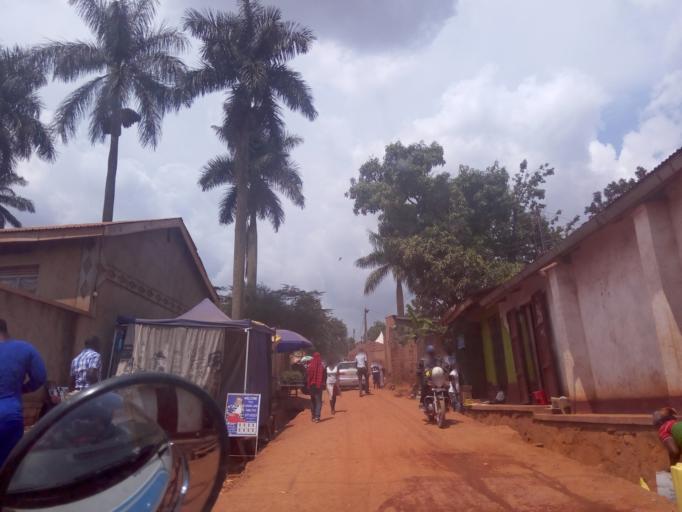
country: UG
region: Central Region
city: Kampala Central Division
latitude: 0.3473
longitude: 32.5609
